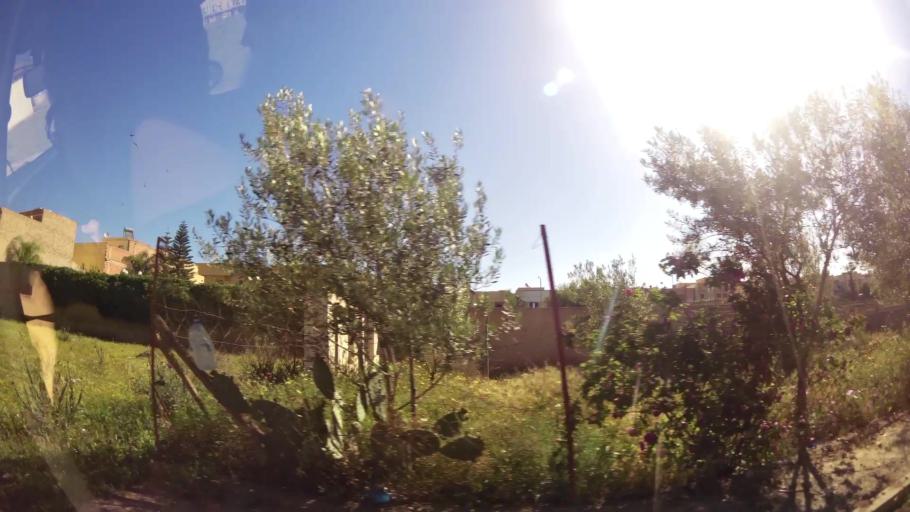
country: MA
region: Oriental
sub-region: Oujda-Angad
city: Oujda
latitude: 34.6569
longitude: -1.8932
